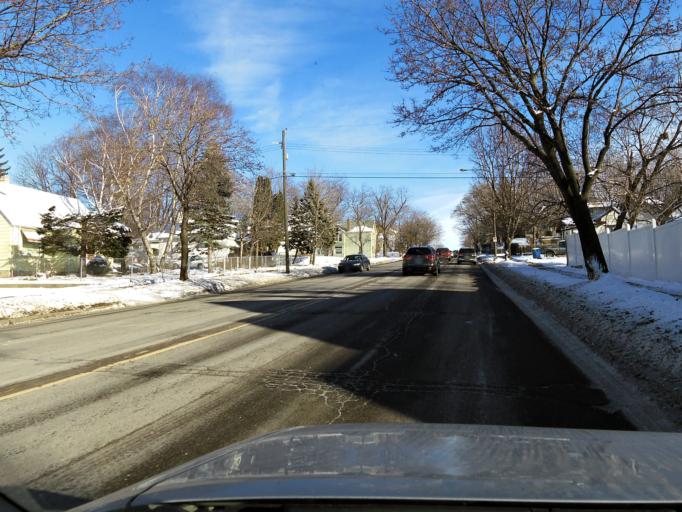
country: US
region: Minnesota
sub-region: Ramsey County
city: Saint Paul
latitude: 44.9773
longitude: -93.0797
